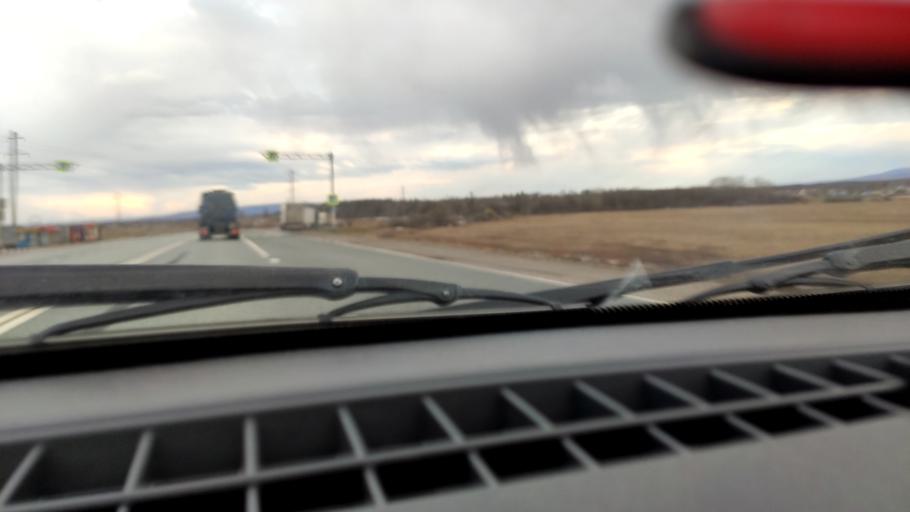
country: RU
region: Bashkortostan
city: Kudeyevskiy
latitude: 54.8168
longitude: 56.7345
